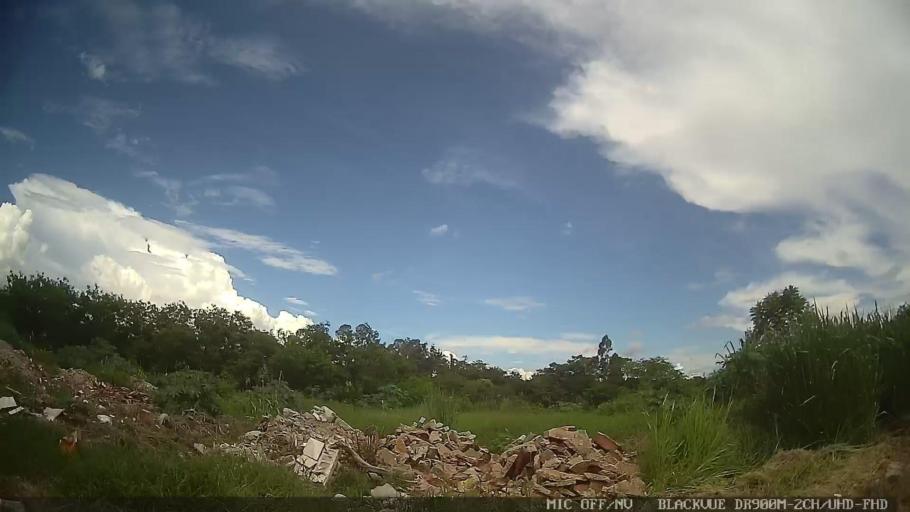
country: BR
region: Sao Paulo
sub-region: Conchas
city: Conchas
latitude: -23.0085
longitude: -48.0039
